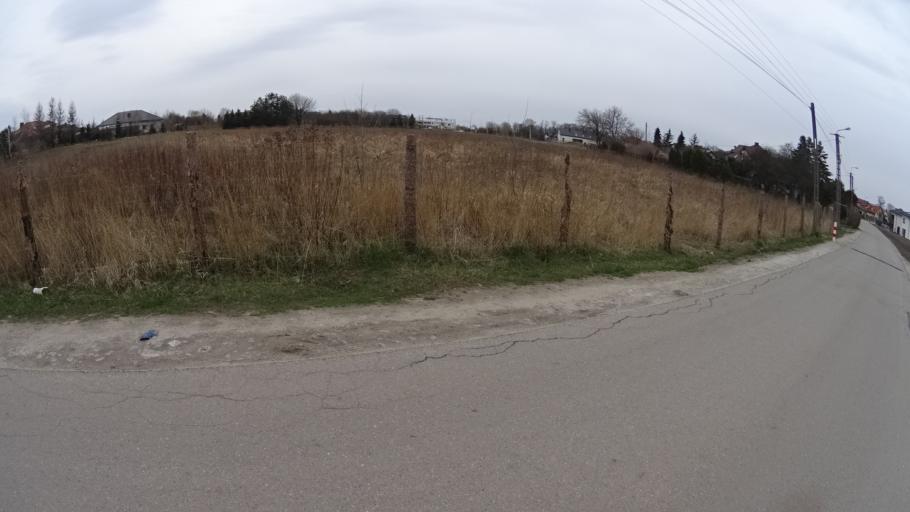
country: PL
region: Masovian Voivodeship
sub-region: Powiat warszawski zachodni
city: Stare Babice
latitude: 52.2483
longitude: 20.8253
